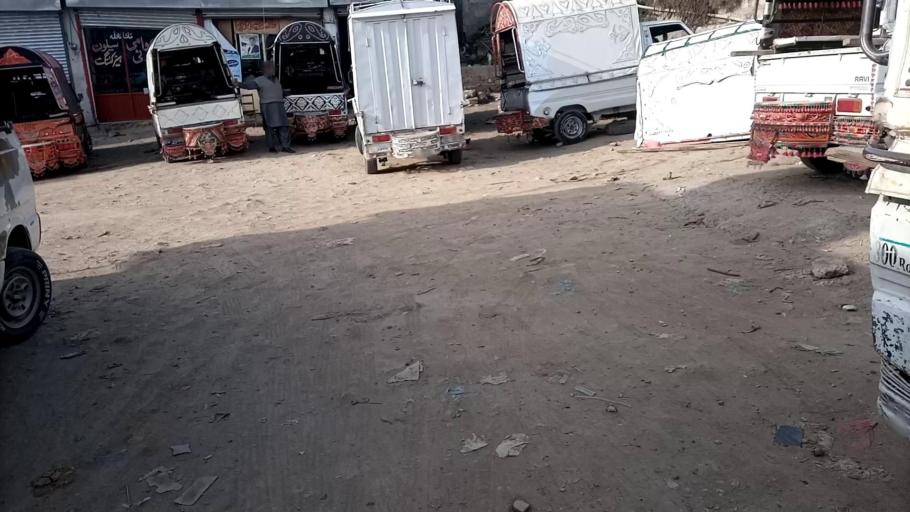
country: PK
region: Khyber Pakhtunkhwa
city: Abbottabad
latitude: 34.2197
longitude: 73.2446
